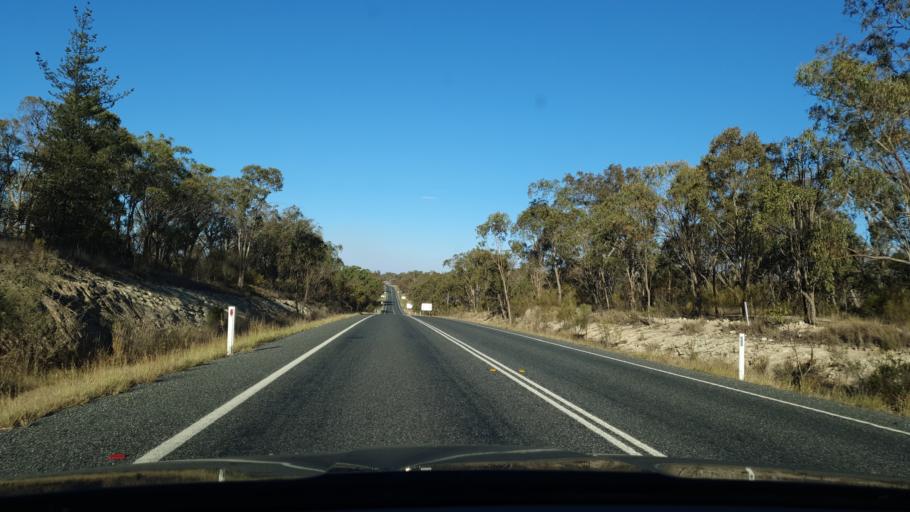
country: AU
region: Queensland
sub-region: Southern Downs
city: Stanthorpe
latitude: -28.6412
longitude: 151.9390
